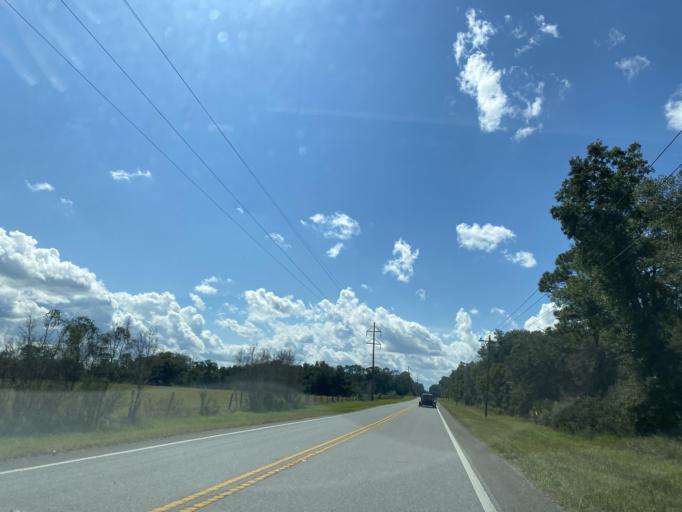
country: US
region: Florida
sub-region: Lake County
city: Umatilla
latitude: 28.9719
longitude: -81.5577
